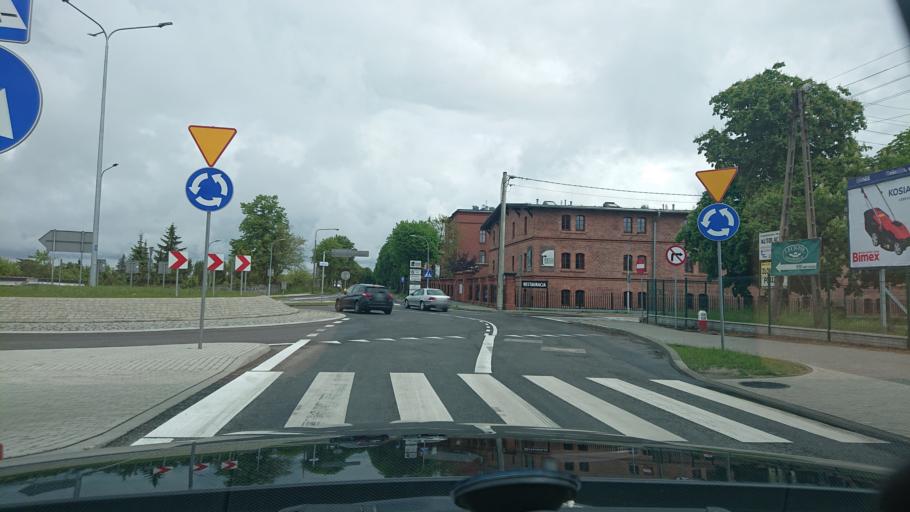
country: PL
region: Greater Poland Voivodeship
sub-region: Powiat gnieznienski
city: Gniezno
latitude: 52.5137
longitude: 17.5952
